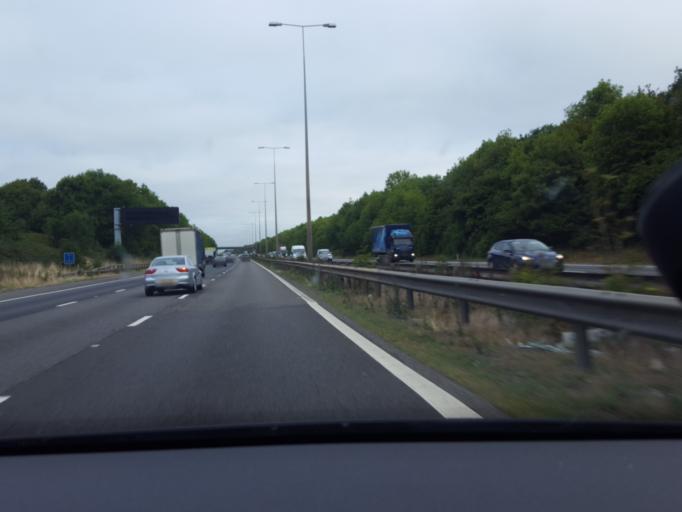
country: GB
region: England
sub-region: Leicestershire
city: Shepshed
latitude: 52.7859
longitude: -1.2852
